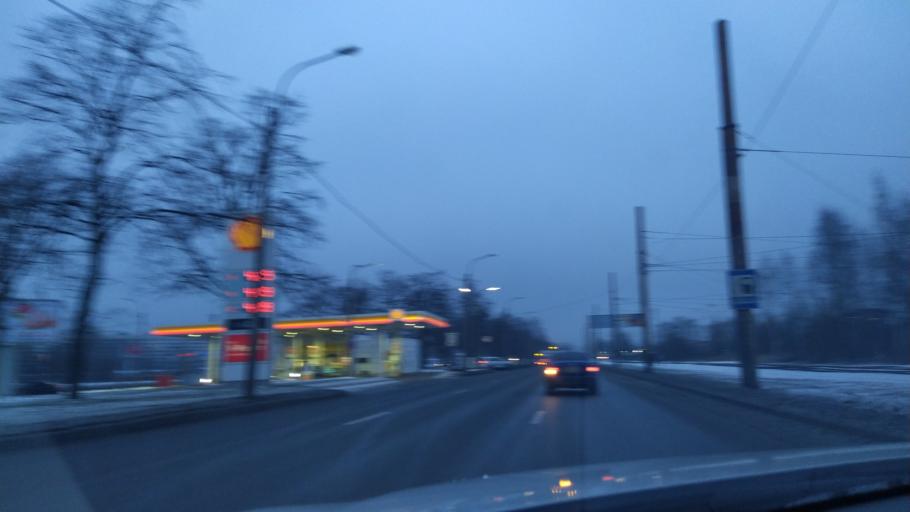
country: RU
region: St.-Petersburg
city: Grazhdanka
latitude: 60.0195
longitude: 30.4327
